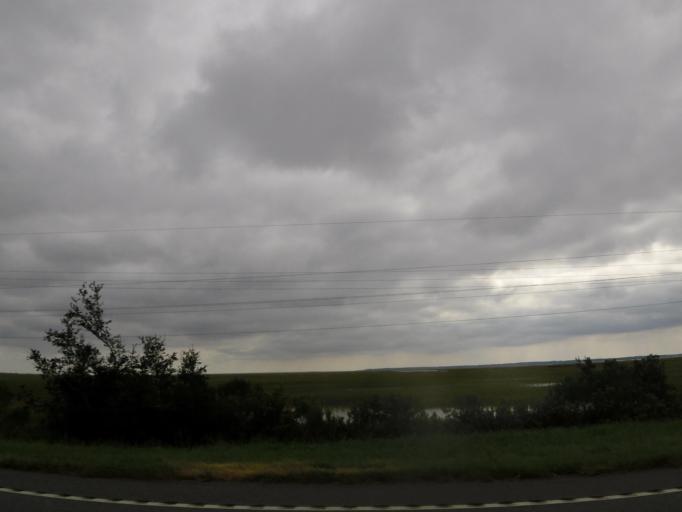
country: US
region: Georgia
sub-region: Glynn County
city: Brunswick
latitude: 31.0690
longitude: -81.4599
